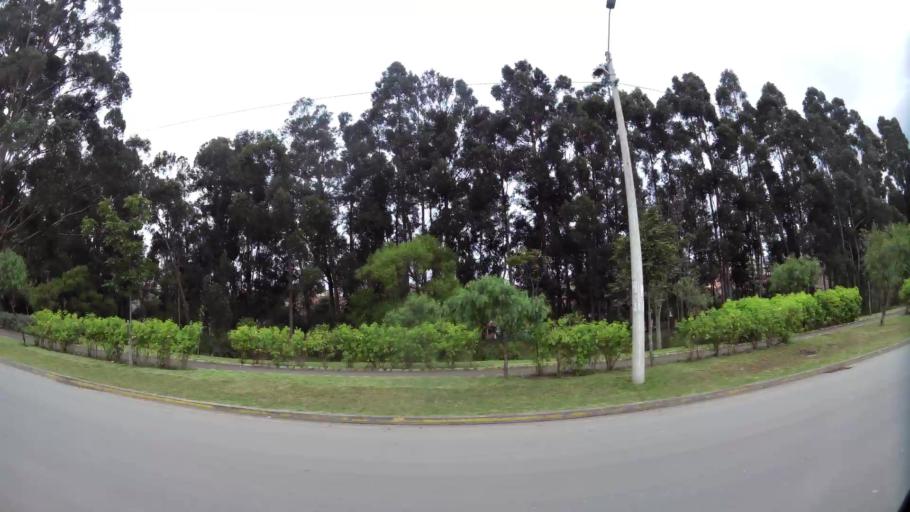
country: EC
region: Azuay
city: Cuenca
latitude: -2.8971
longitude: -78.9708
